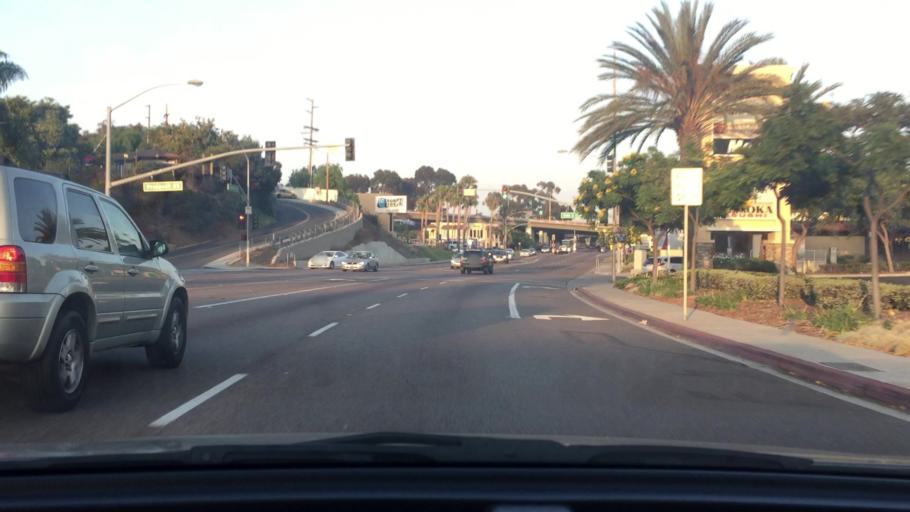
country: US
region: California
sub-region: San Diego County
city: Chula Vista
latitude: 32.6615
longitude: -117.0812
